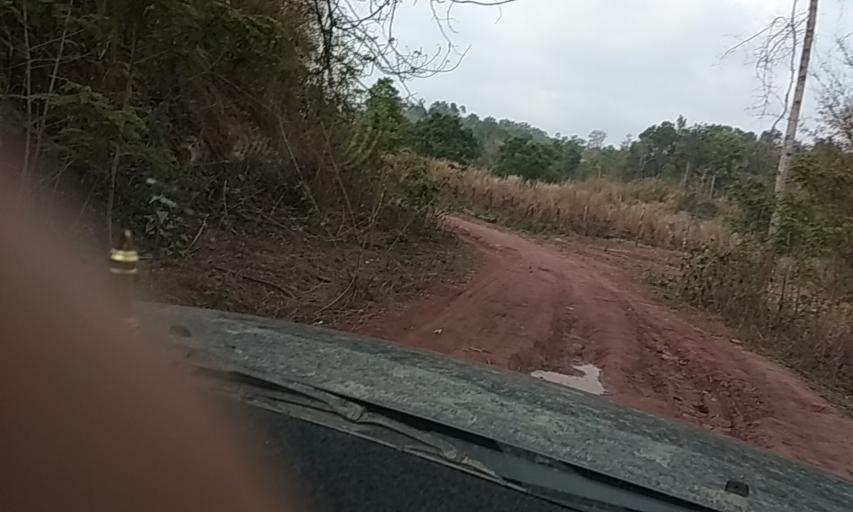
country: TH
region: Nan
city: Mae Charim
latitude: 18.4493
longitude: 101.1960
